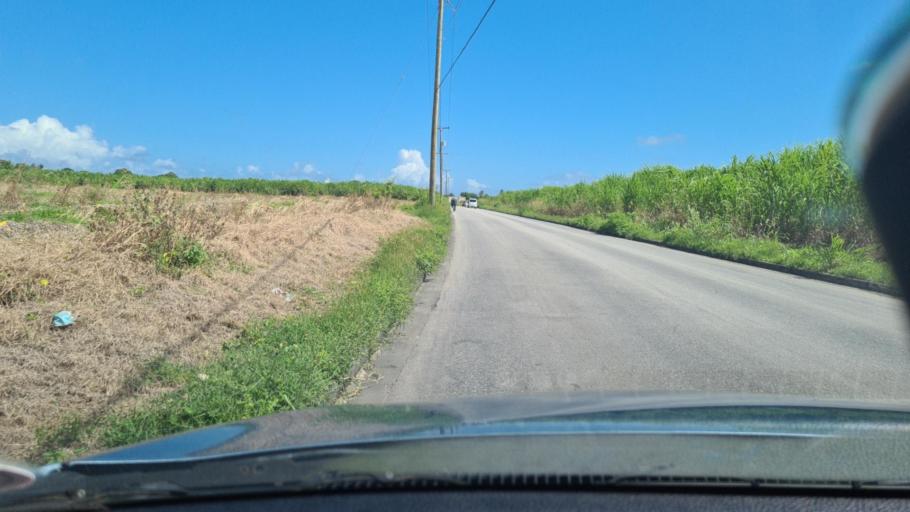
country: BB
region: Saint Philip
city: Crane
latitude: 13.1183
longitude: -59.4597
